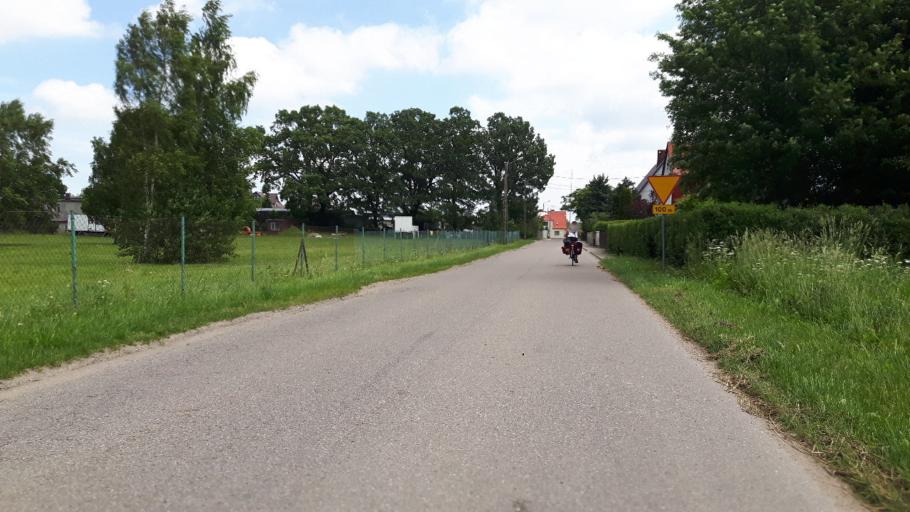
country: PL
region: Pomeranian Voivodeship
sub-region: Powiat wejherowski
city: Choczewo
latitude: 54.7416
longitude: 17.8882
